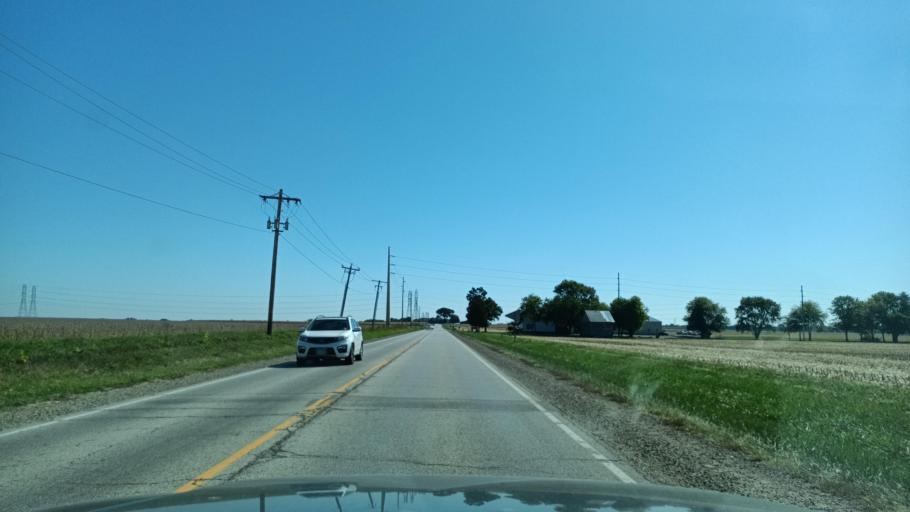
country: US
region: Illinois
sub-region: Peoria County
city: Dunlap
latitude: 40.7893
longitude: -89.7443
